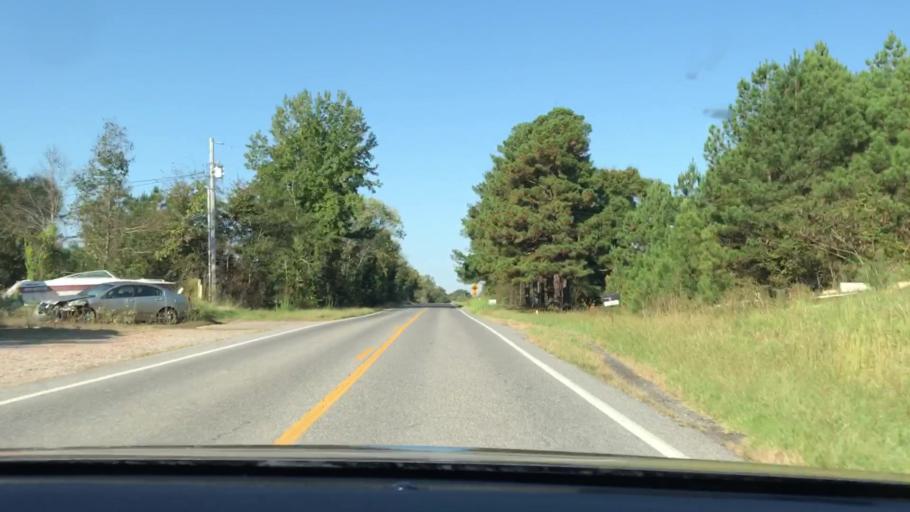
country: US
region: Kentucky
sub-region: Marshall County
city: Benton
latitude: 36.7639
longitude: -88.2026
